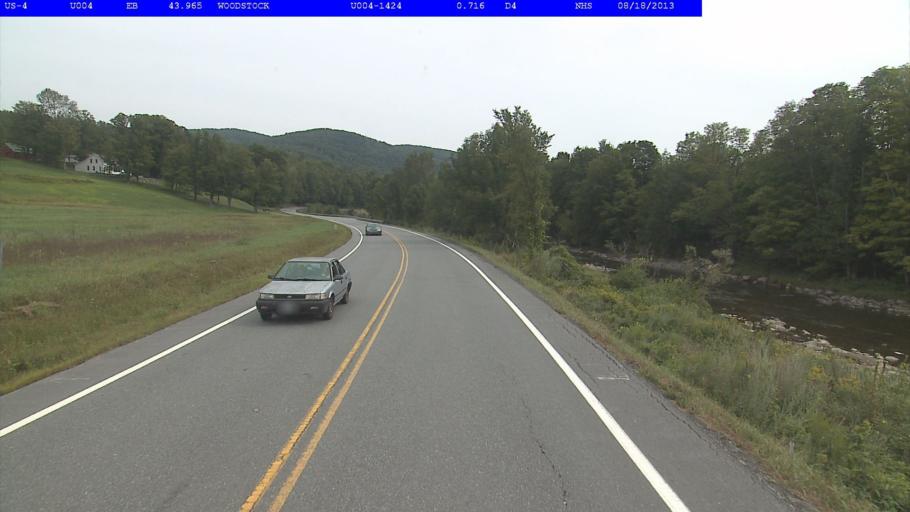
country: US
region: Vermont
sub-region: Windsor County
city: Woodstock
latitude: 43.5907
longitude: -72.6089
